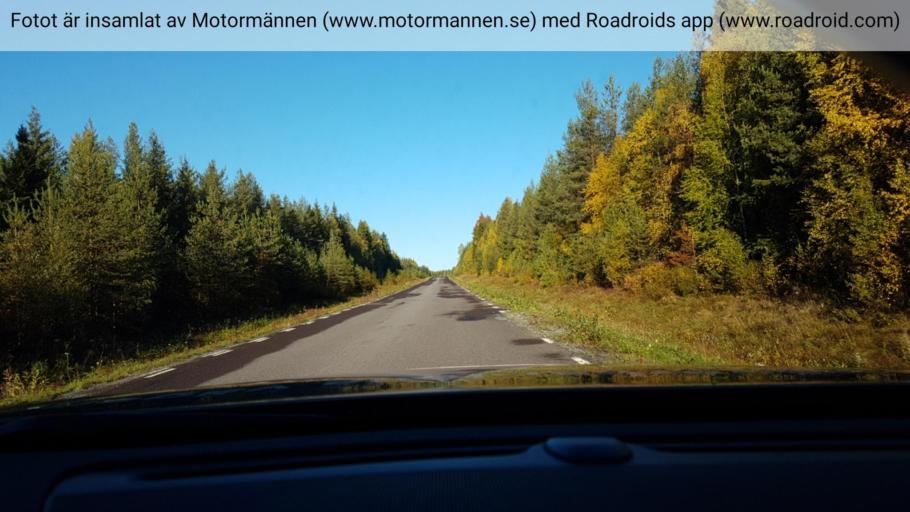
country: SE
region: Norrbotten
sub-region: Bodens Kommun
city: Boden
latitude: 66.0554
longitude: 21.4463
